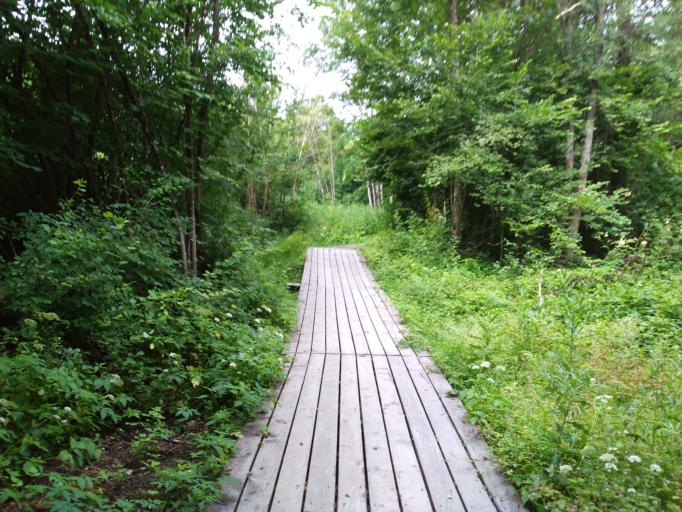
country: CH
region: Grisons
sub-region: Surselva District
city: Laax
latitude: 46.7813
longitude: 9.2521
